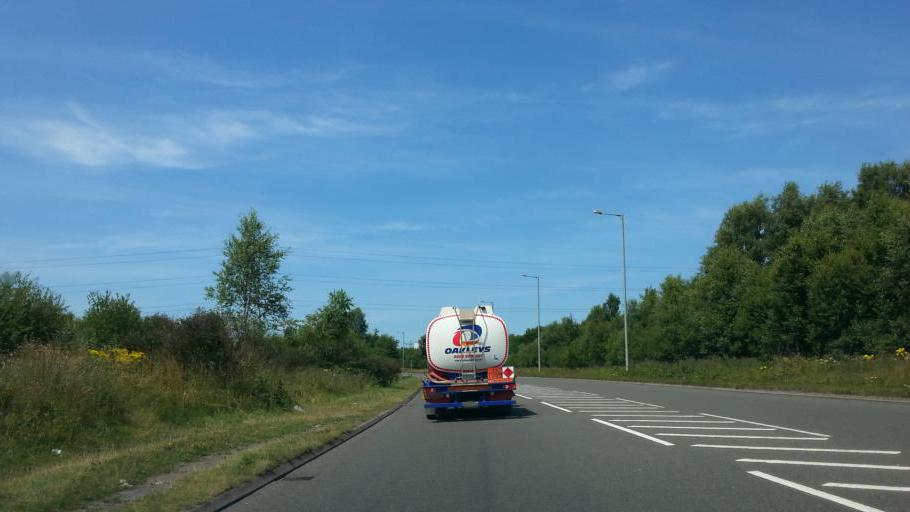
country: GB
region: England
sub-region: Staffordshire
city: Norton Canes
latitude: 52.6773
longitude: -1.9470
